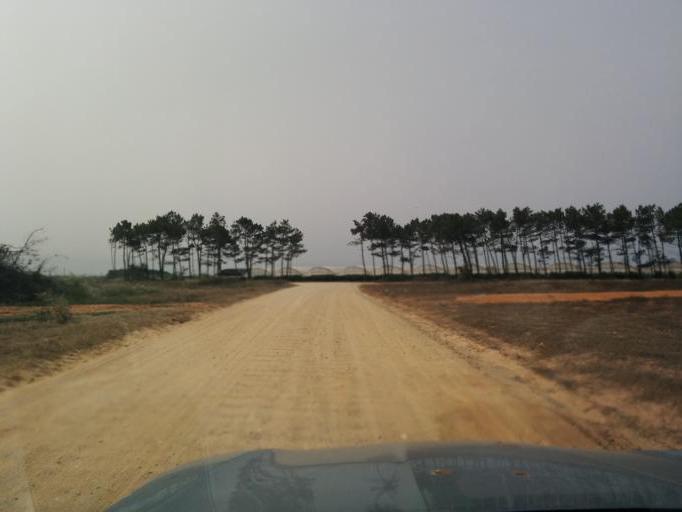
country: PT
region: Beja
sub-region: Odemira
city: Sao Teotonio
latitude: 37.5094
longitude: -8.7846
